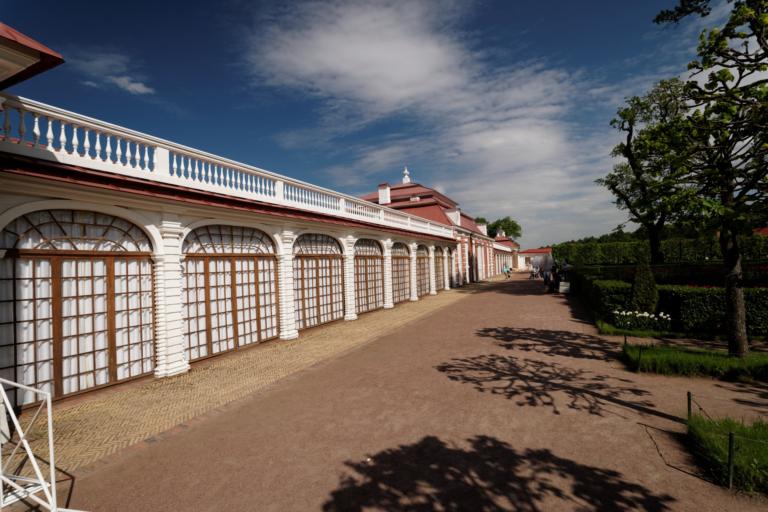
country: RU
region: St.-Petersburg
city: Peterhof
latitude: 59.8872
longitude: 29.9186
